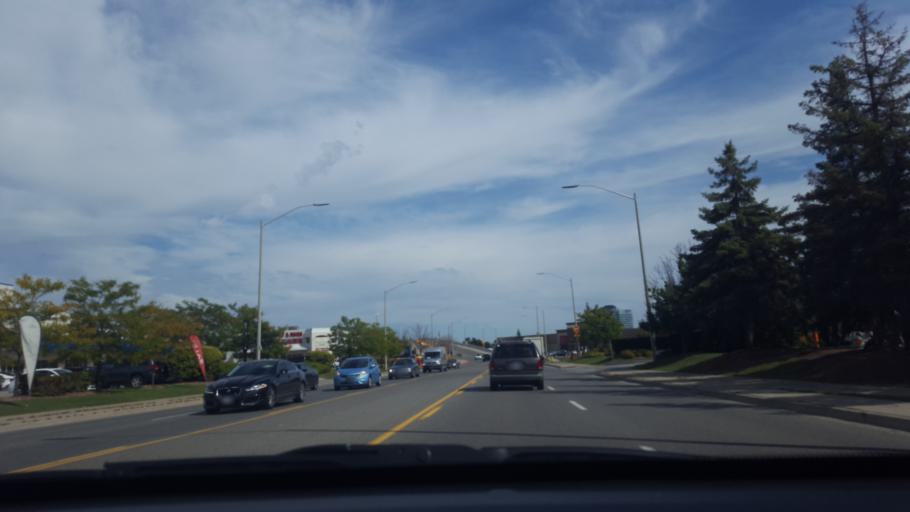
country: CA
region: Ontario
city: Concord
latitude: 43.7934
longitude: -79.5461
